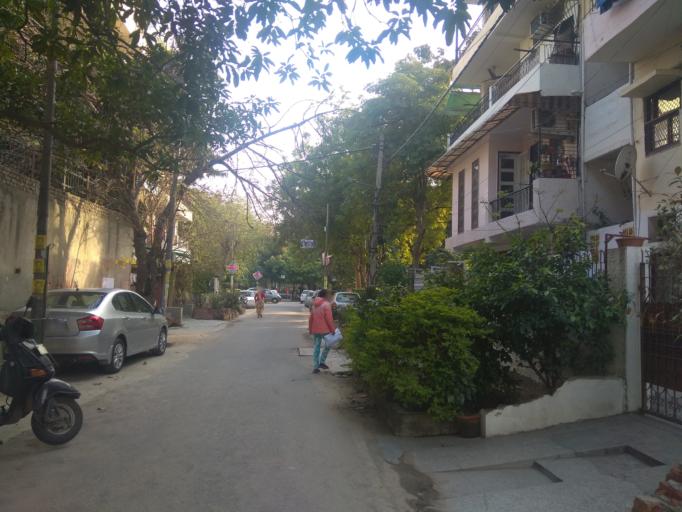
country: IN
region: NCT
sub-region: West Delhi
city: Nangloi Jat
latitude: 28.6287
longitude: 77.0665
